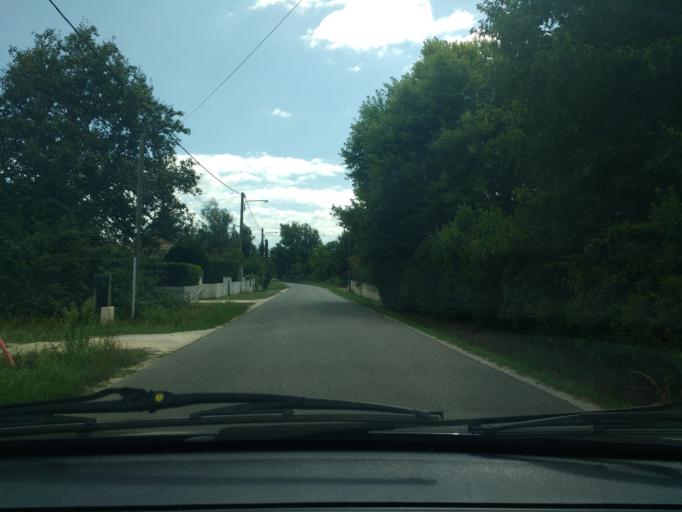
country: FR
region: Aquitaine
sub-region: Departement de la Gironde
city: Salles
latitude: 44.5586
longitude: -0.8559
